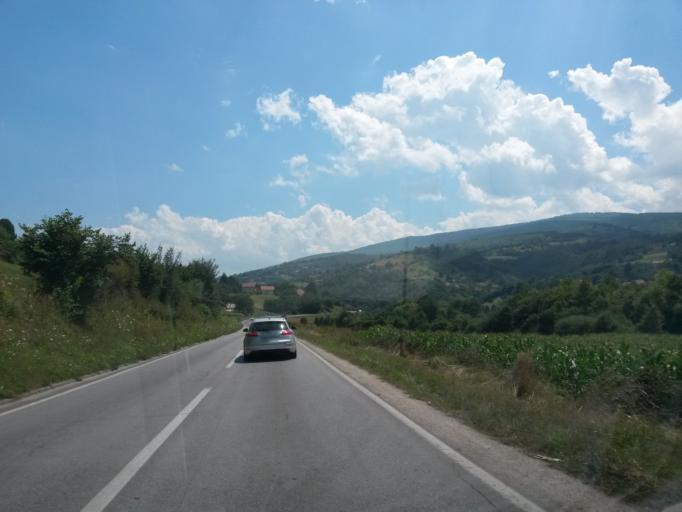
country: BA
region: Federation of Bosnia and Herzegovina
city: Turbe
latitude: 44.2377
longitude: 17.6077
